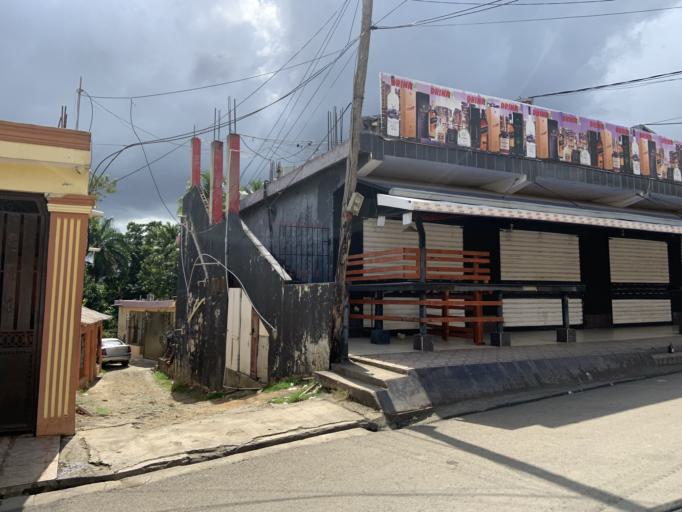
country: DO
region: Monte Plata
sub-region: Yamasa
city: Yamasa
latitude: 18.7736
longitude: -70.0232
